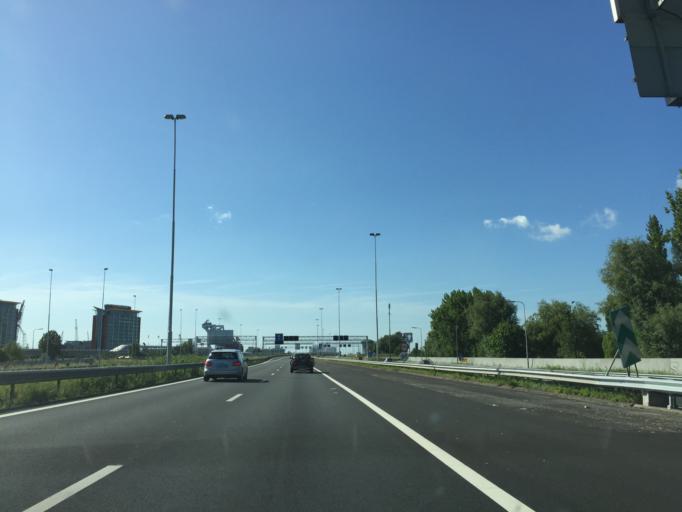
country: NL
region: South Holland
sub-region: Gemeente Schiedam
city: Schiedam
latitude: 51.9128
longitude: 4.3683
